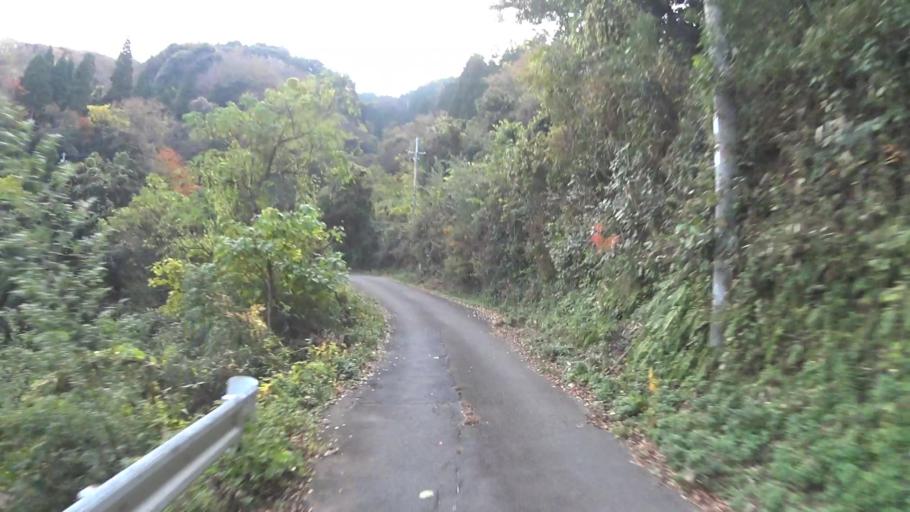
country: JP
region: Kyoto
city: Maizuru
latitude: 35.5610
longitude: 135.4626
